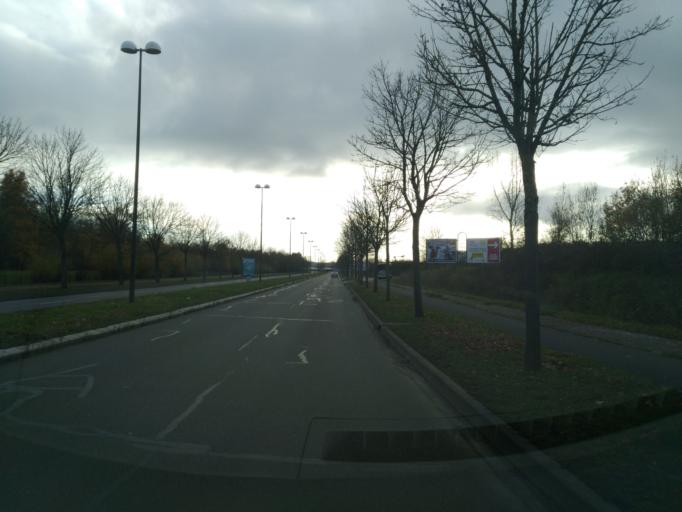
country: FR
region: Ile-de-France
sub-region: Departement des Yvelines
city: Guyancourt
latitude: 48.7697
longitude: 2.0819
